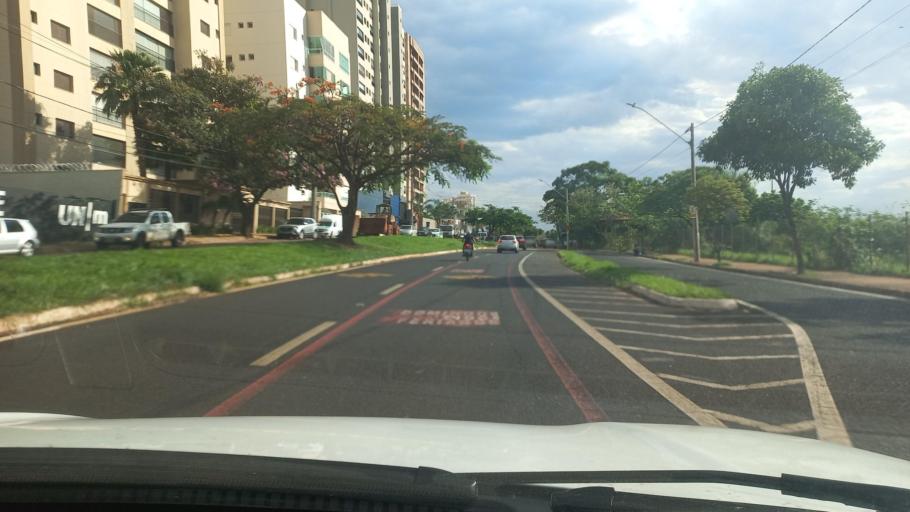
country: BR
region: Minas Gerais
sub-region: Uberaba
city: Uberaba
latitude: -19.7500
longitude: -47.9115
